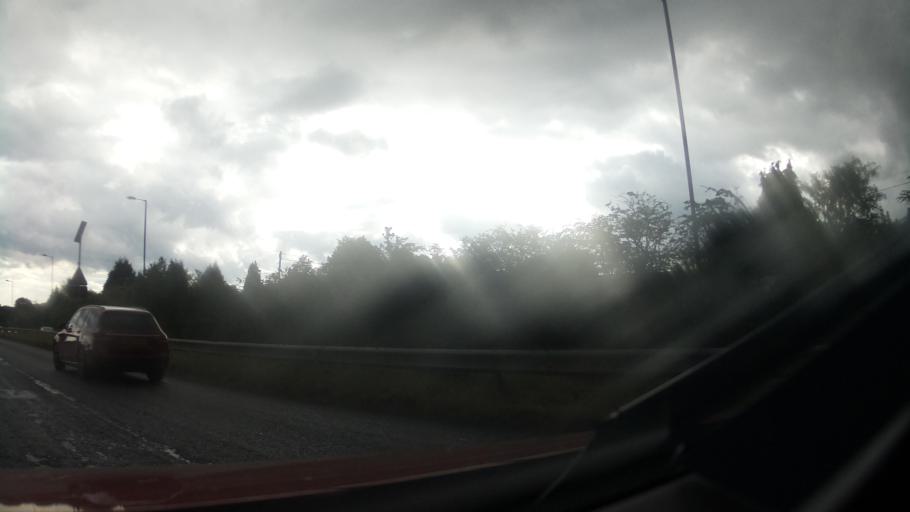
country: GB
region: England
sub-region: Dudley
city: Kingswinford
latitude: 52.5463
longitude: -2.1716
